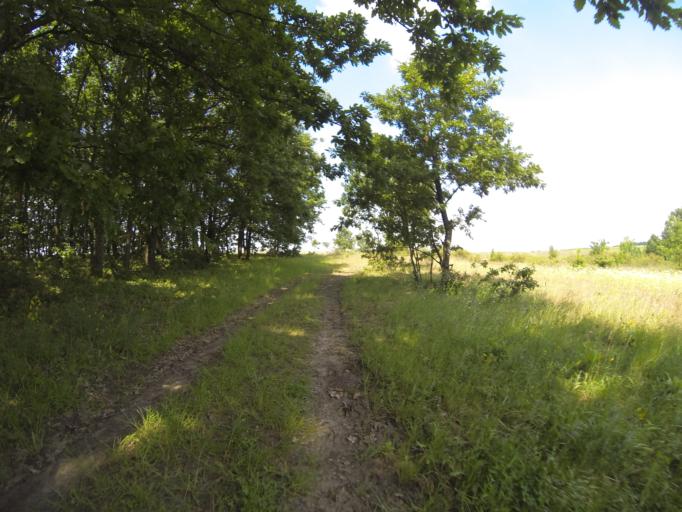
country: RO
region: Gorj
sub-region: Comuna Crusetu
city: Crusetu
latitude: 44.6148
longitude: 23.6269
